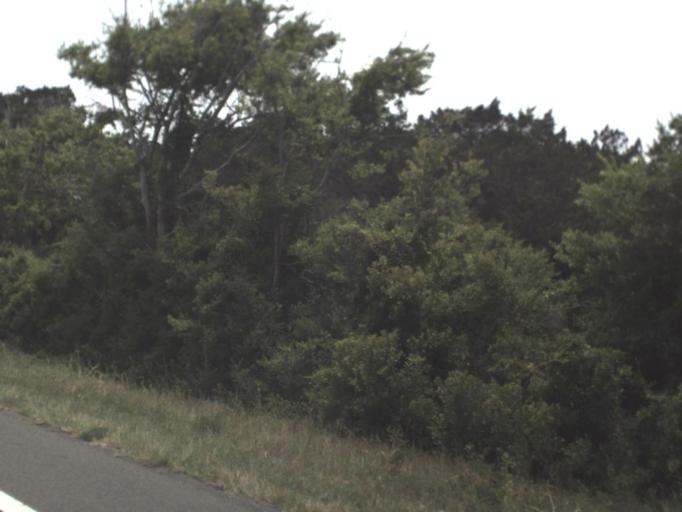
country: US
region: Florida
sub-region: Nassau County
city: Fernandina Beach
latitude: 30.5088
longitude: -81.4581
